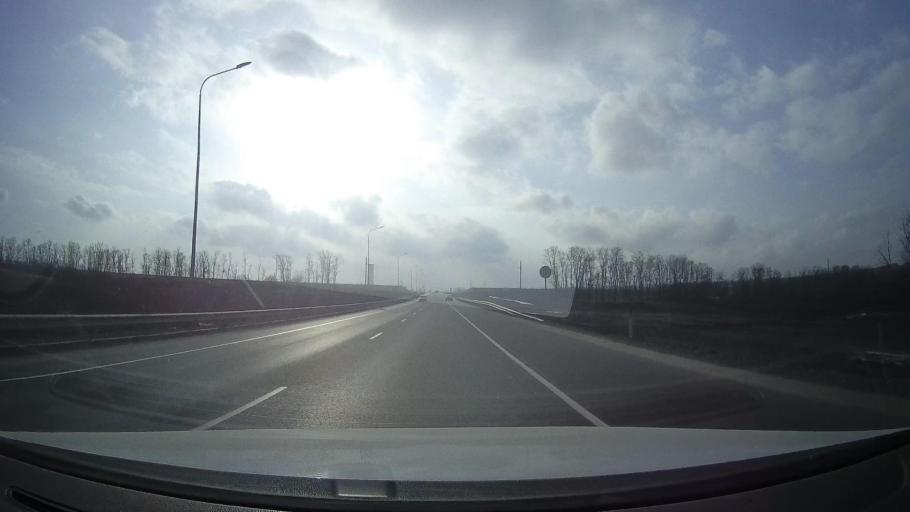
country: RU
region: Rostov
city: Grushevskaya
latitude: 47.4196
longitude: 39.8623
